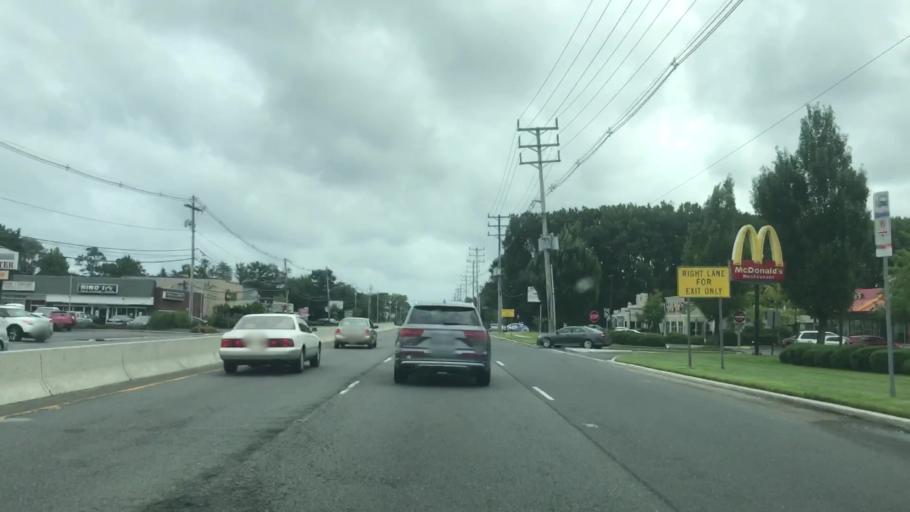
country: US
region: New Jersey
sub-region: Monmouth County
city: Oakhurst
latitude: 40.2643
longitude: -74.0421
